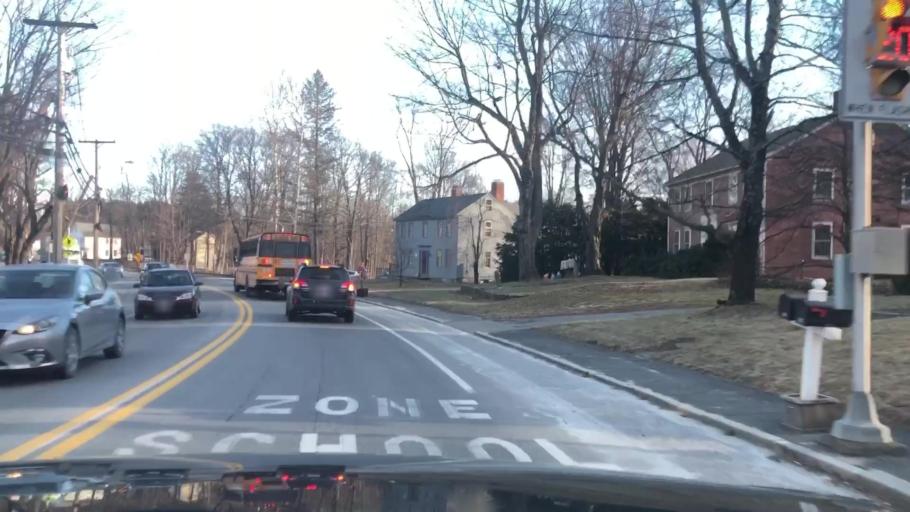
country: US
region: Massachusetts
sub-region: Worcester County
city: Bolton
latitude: 42.4335
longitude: -71.6088
